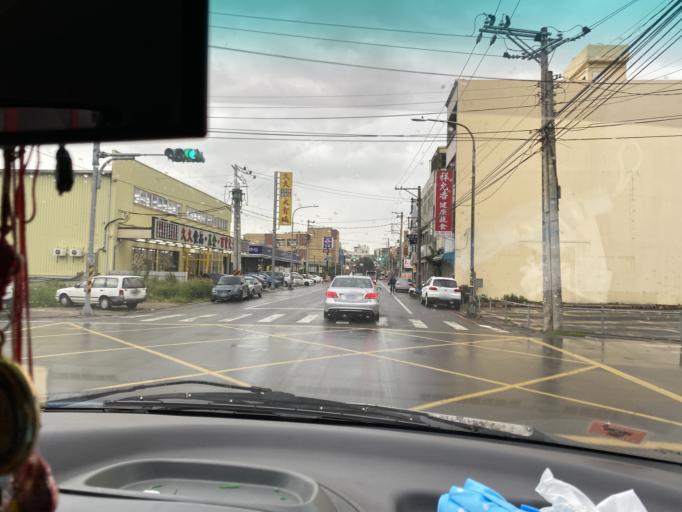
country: TW
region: Taiwan
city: Taoyuan City
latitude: 25.0610
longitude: 121.1996
